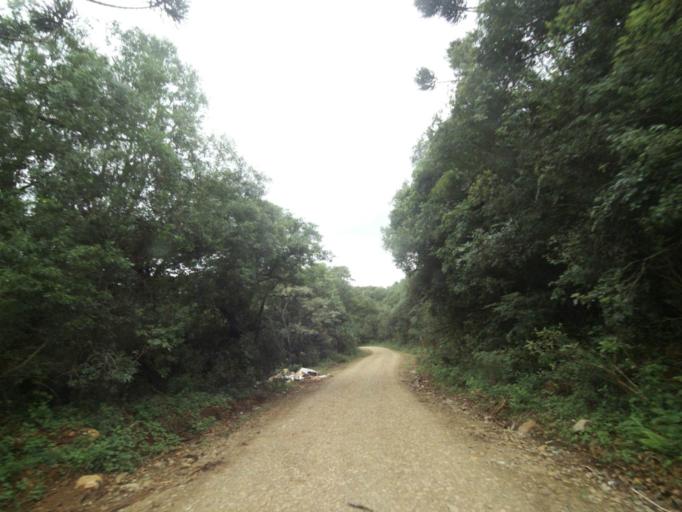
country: BR
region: Rio Grande do Sul
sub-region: Lagoa Vermelha
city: Lagoa Vermelha
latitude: -28.1983
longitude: -51.5352
